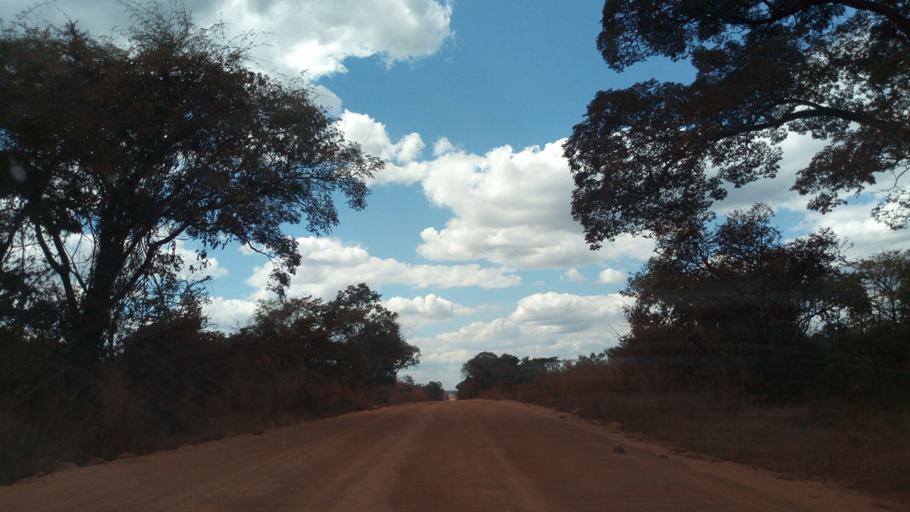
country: ZM
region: Copperbelt
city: Mufulira
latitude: -12.0289
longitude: 28.6745
